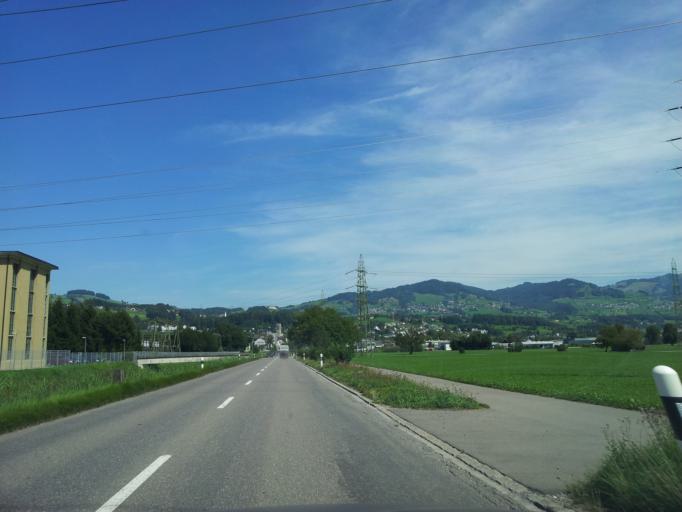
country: CH
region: Saint Gallen
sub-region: Wahlkreis See-Gaster
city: Uznach
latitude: 47.2183
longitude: 8.9730
